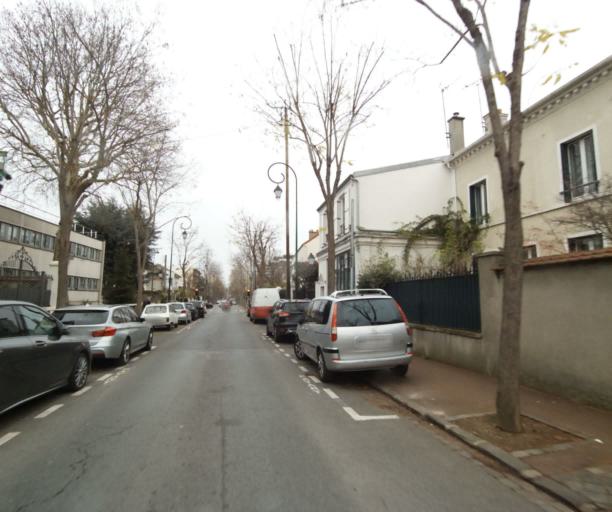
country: FR
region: Ile-de-France
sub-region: Departement des Hauts-de-Seine
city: Rueil-Malmaison
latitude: 48.8831
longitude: 2.1758
